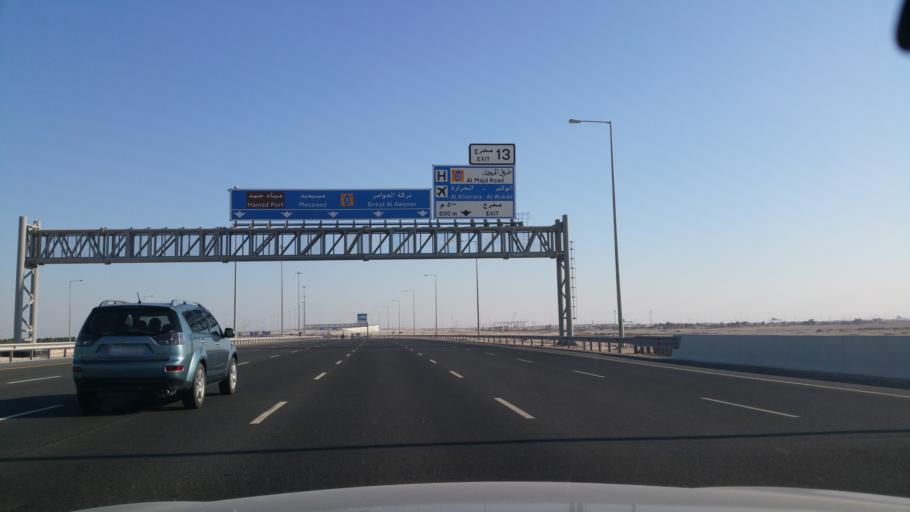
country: QA
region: Al Wakrah
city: Al Wukayr
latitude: 25.1351
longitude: 51.4779
